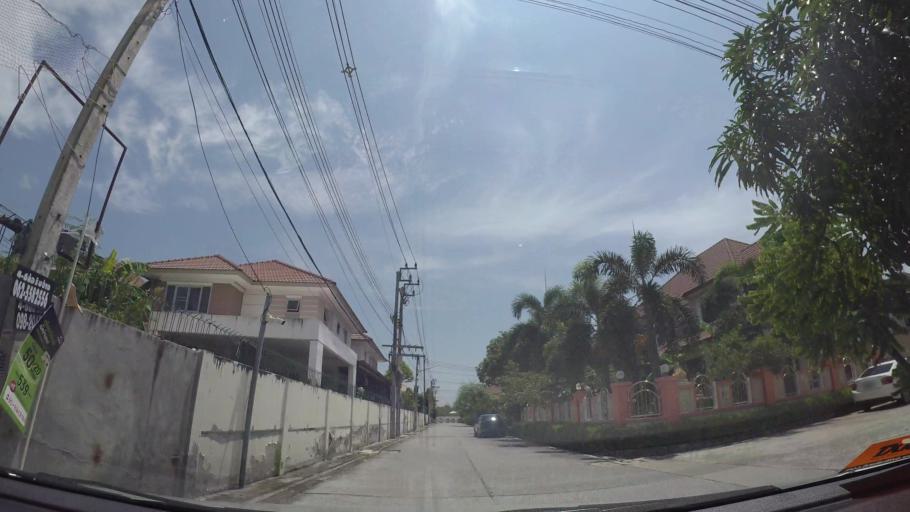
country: TH
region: Chon Buri
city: Chon Buri
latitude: 13.3290
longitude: 100.9438
